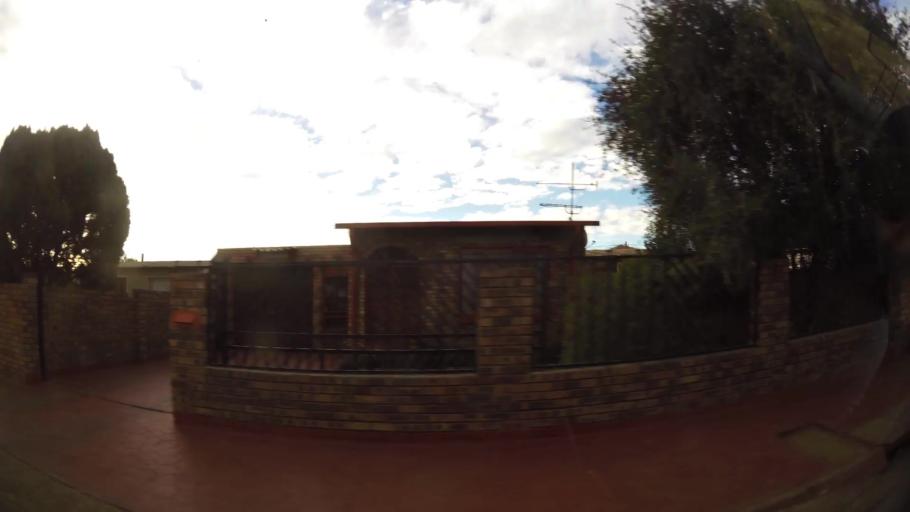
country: ZA
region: Gauteng
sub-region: City of Tshwane Metropolitan Municipality
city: Pretoria
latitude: -25.7136
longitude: 28.3245
